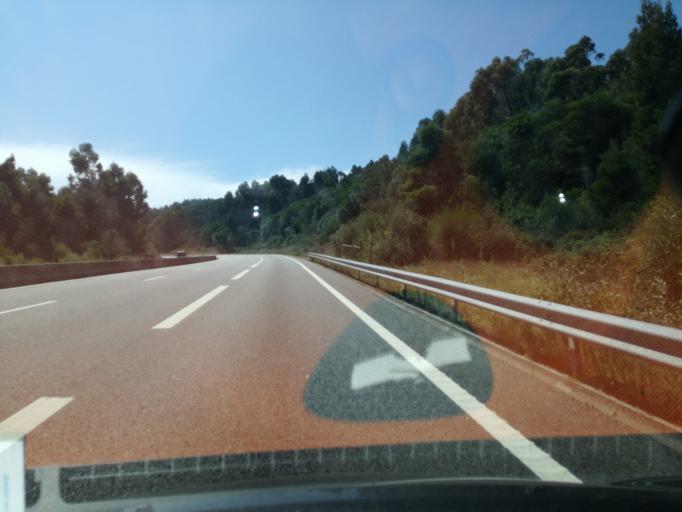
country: PT
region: Viana do Castelo
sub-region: Caminha
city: Vila Praia de Ancora
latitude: 41.7839
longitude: -8.7888
